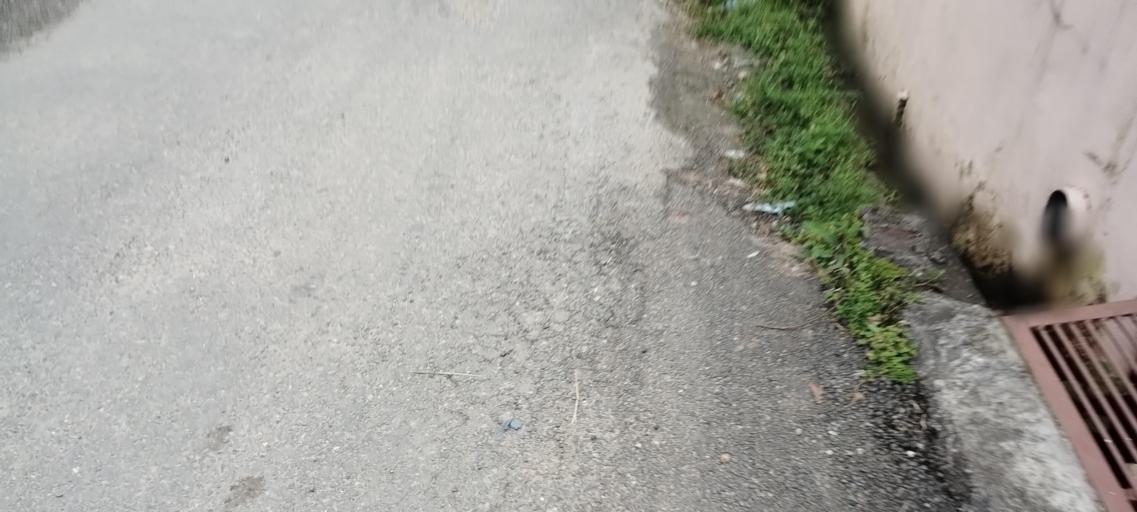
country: NP
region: Central Region
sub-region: Bagmati Zone
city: Kathmandu
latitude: 27.7827
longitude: 85.3630
